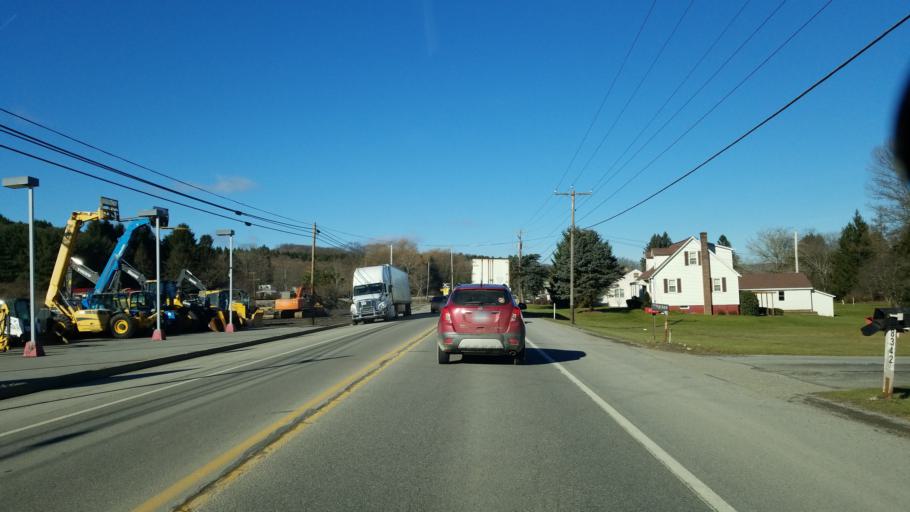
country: US
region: Pennsylvania
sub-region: Jefferson County
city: Brockway
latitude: 41.2250
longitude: -78.7794
